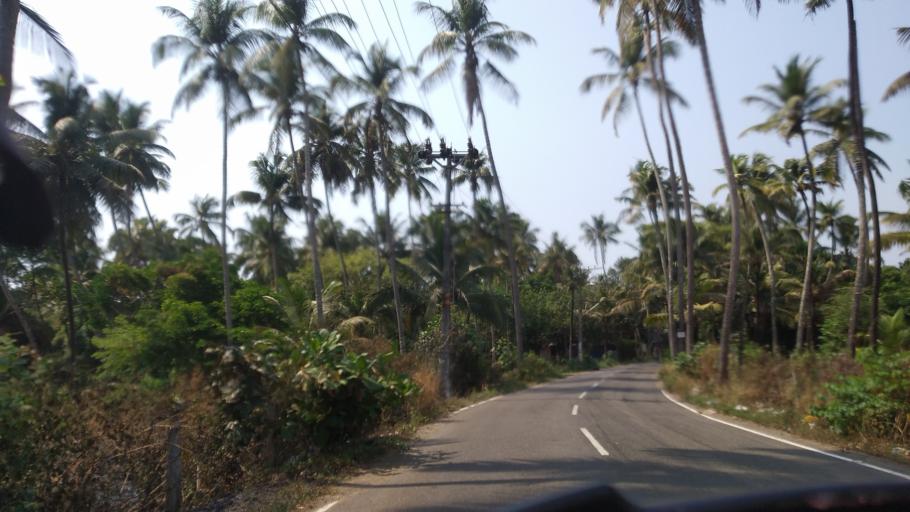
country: IN
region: Kerala
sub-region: Thrissur District
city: Thanniyam
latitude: 10.3797
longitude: 76.1016
